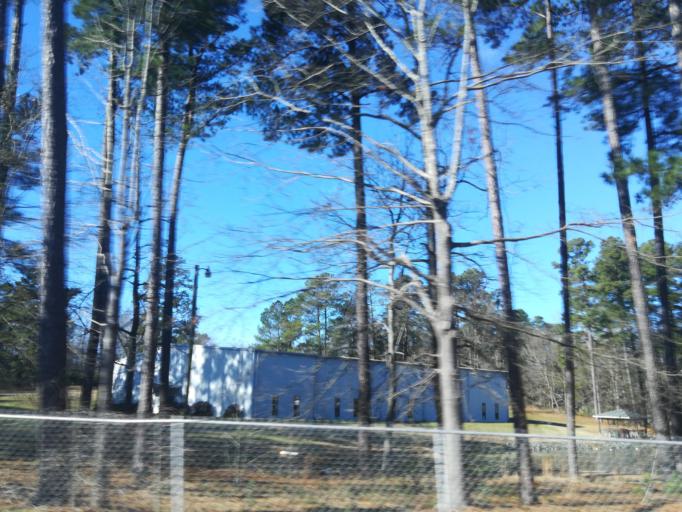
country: US
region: North Carolina
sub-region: Durham County
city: Durham
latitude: 36.0336
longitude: -78.9815
